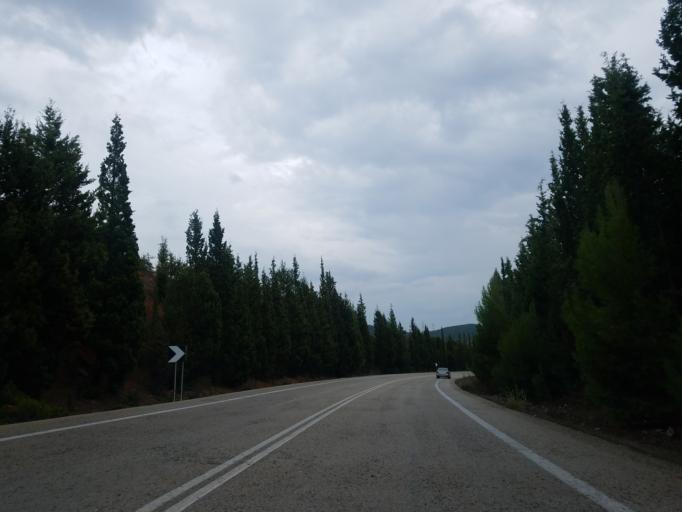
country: GR
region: Central Greece
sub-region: Nomos Voiotias
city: Stirion
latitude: 38.4499
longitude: 22.7873
